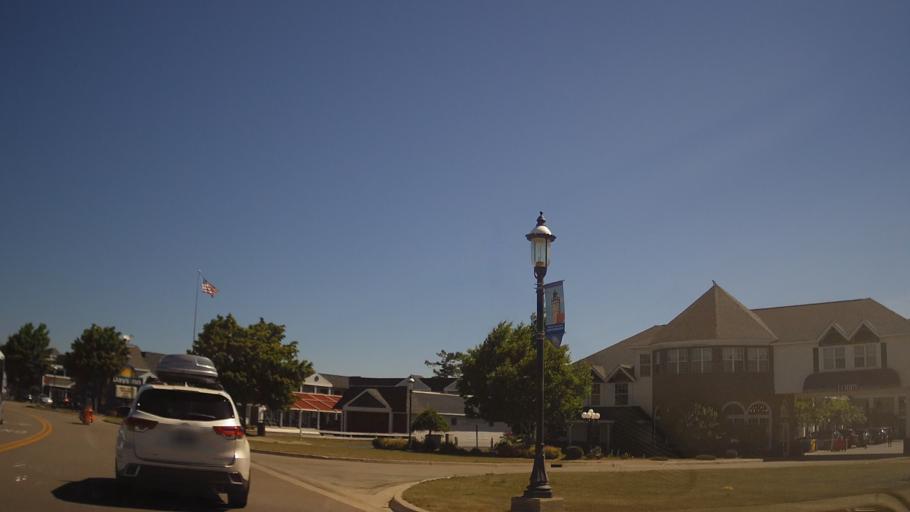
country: US
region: Michigan
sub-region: Mackinac County
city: Saint Ignace
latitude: 45.7706
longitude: -84.7270
